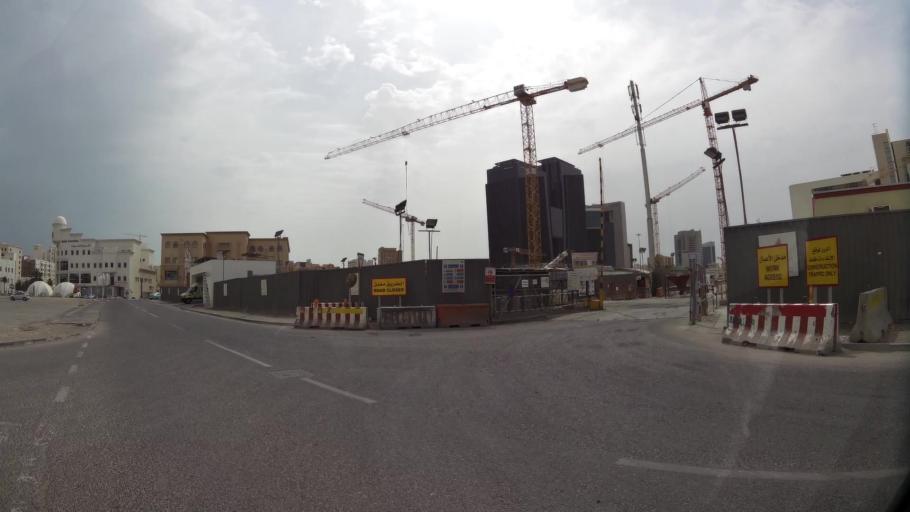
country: QA
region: Baladiyat ad Dawhah
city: Doha
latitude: 25.2831
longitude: 51.5044
